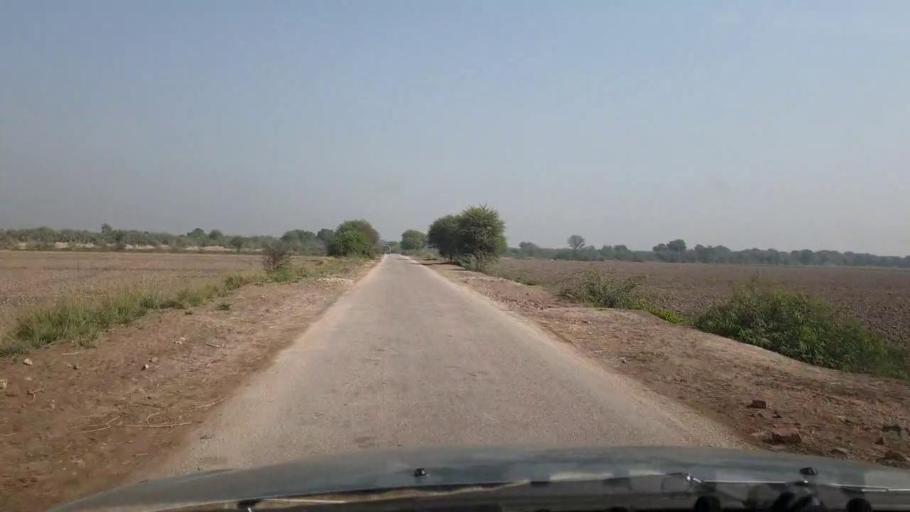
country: PK
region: Sindh
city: Tando Jam
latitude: 25.3041
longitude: 68.5359
